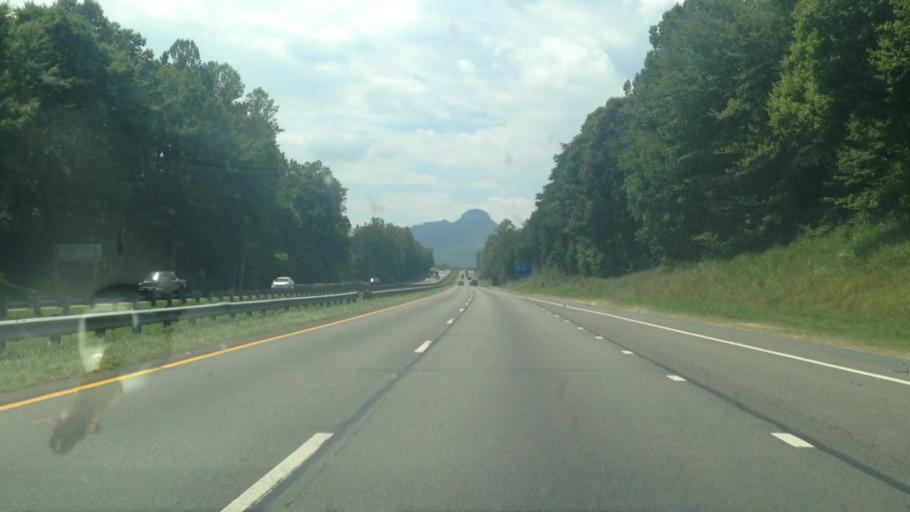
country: US
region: North Carolina
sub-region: Stokes County
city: King
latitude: 36.3099
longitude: -80.4266
